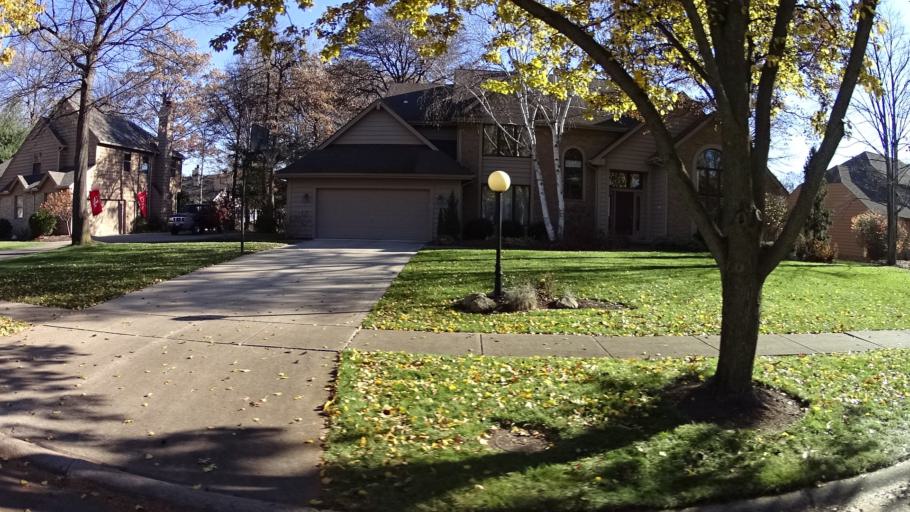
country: US
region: Ohio
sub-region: Lorain County
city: Avon Lake
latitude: 41.4989
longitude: -81.9796
